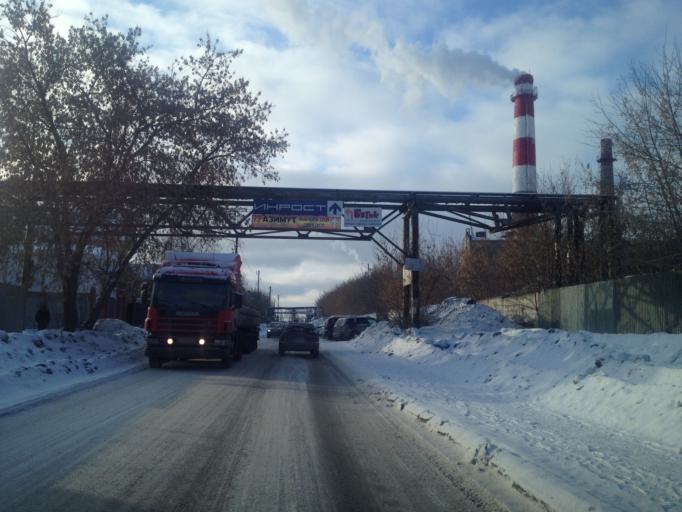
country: RU
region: Sverdlovsk
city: Sovkhoznyy
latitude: 56.7657
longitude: 60.6230
